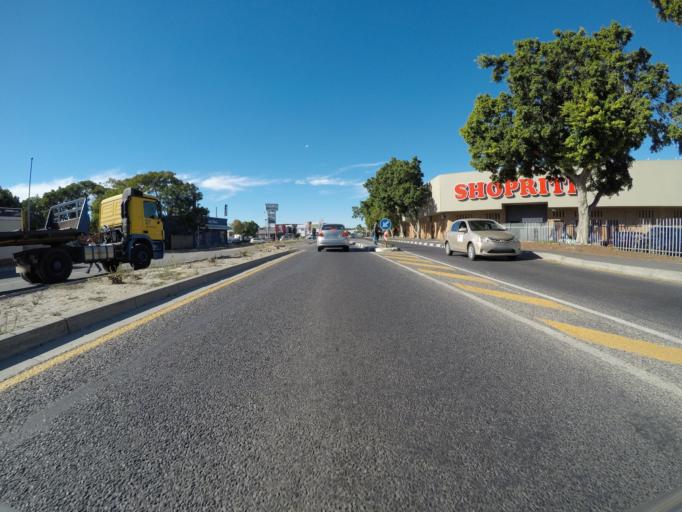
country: ZA
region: Western Cape
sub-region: City of Cape Town
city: Kraaifontein
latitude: -33.9255
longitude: 18.6769
